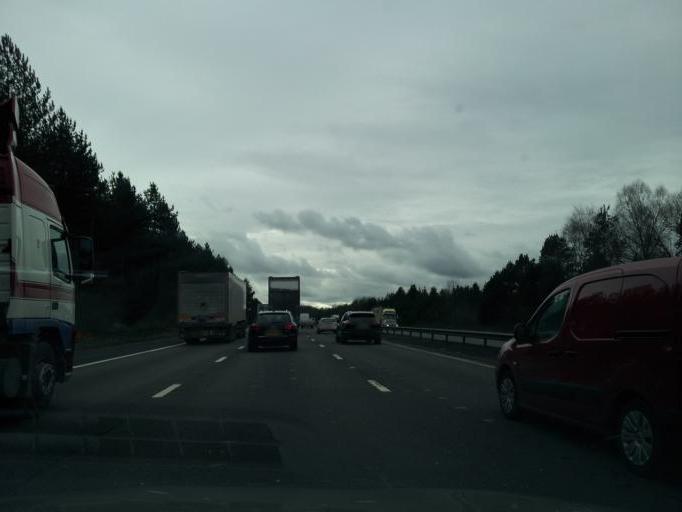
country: GB
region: England
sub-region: Staffordshire
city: Audley
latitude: 53.0176
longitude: -2.3242
